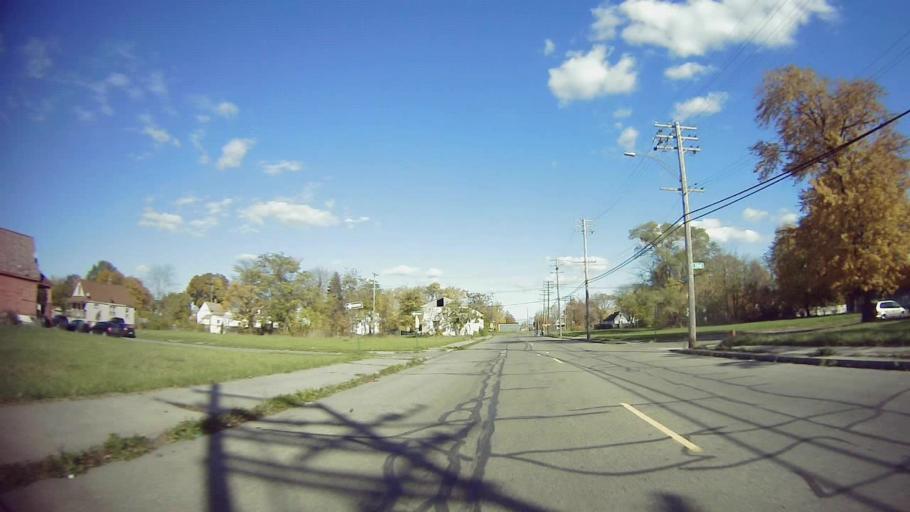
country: US
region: Michigan
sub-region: Wayne County
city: Dearborn
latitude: 42.3353
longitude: -83.1144
